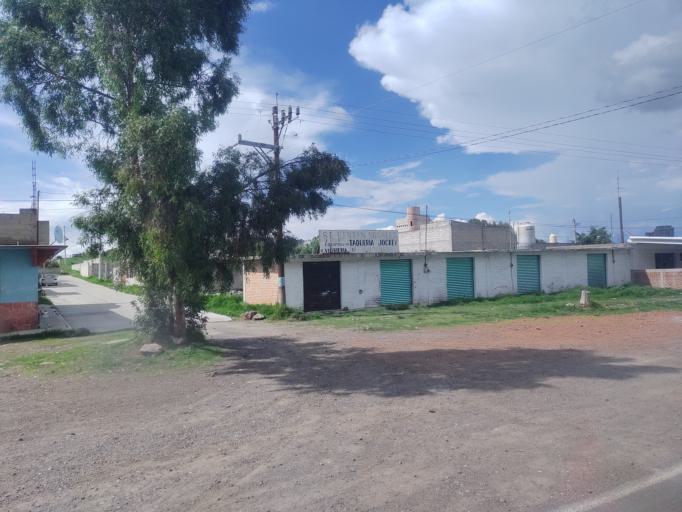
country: MX
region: Mexico
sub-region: Aculco
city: El Colorado
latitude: 20.0962
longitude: -99.7617
